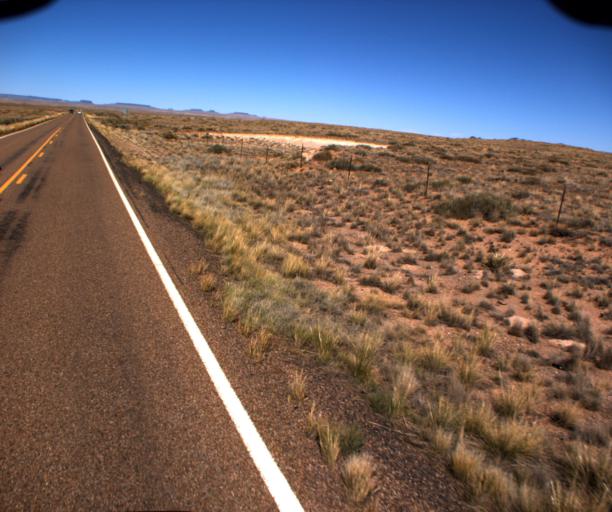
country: US
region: Arizona
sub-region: Navajo County
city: Holbrook
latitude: 35.0081
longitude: -110.0897
